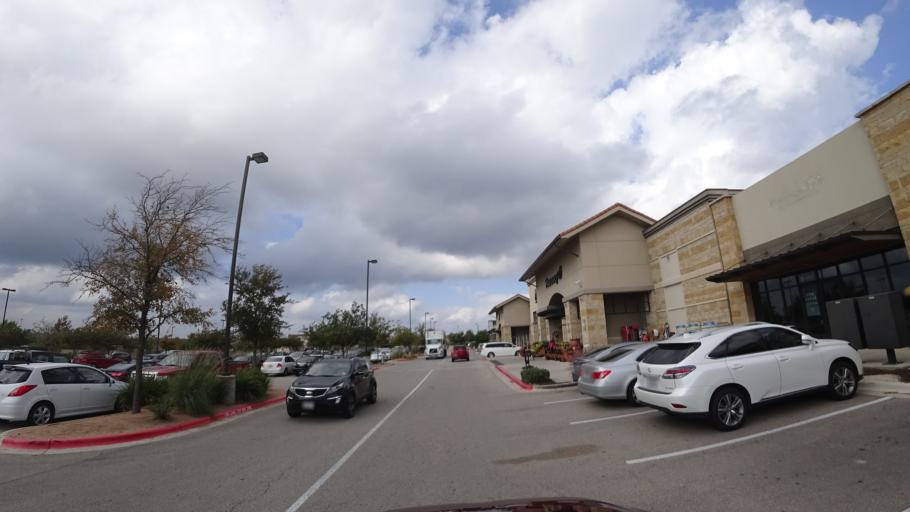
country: US
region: Texas
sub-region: Travis County
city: Hudson Bend
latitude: 30.3885
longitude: -97.8838
